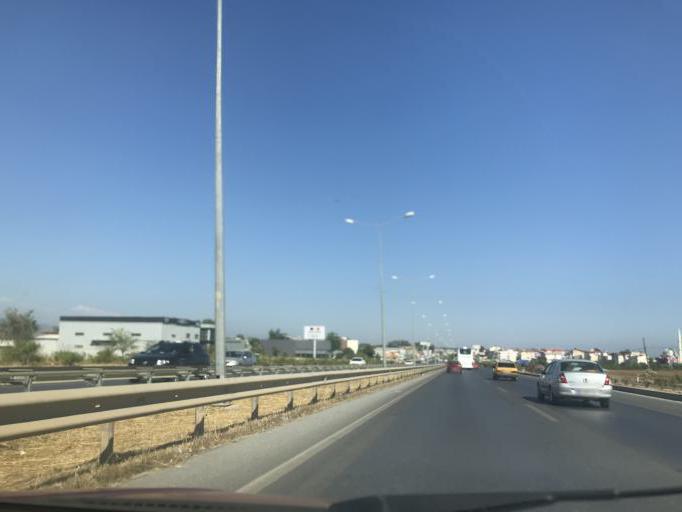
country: TR
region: Antalya
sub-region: Manavgat
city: Side
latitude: 36.8033
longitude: 31.3951
